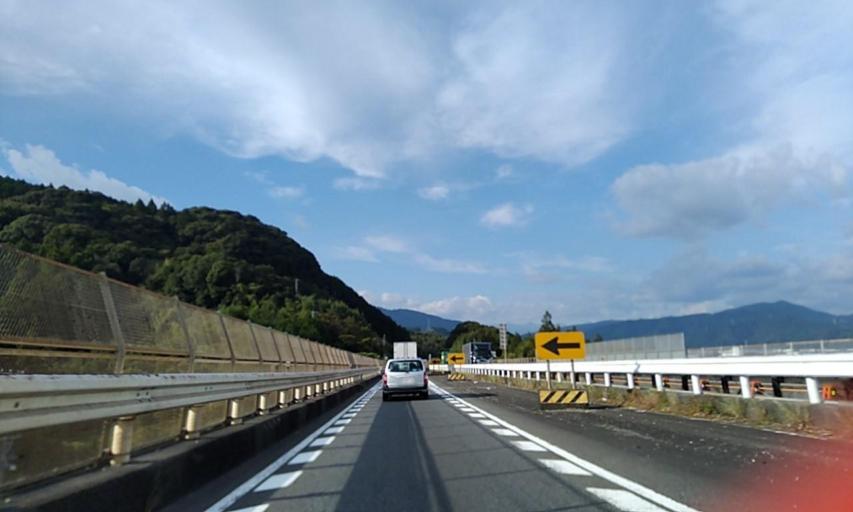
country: JP
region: Shizuoka
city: Kanaya
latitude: 34.8305
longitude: 138.1188
